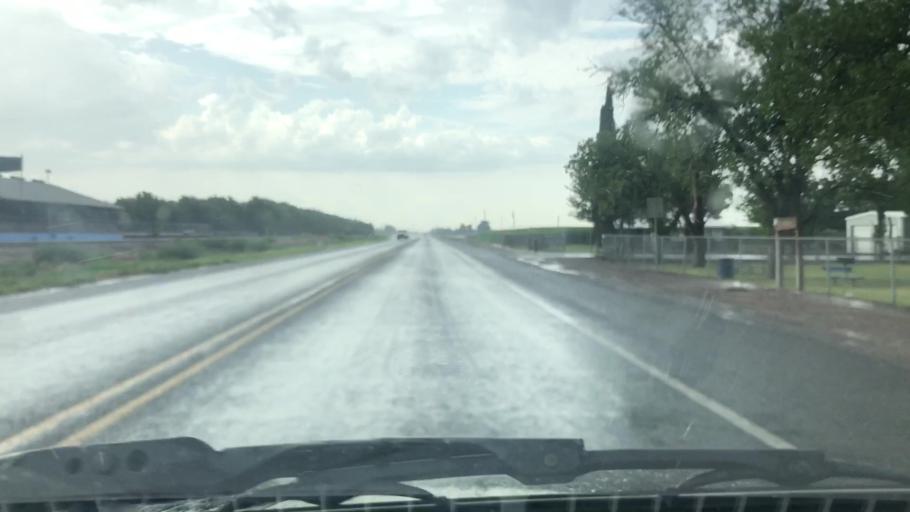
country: US
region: New Mexico
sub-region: Dona Ana County
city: Mesquite
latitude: 32.1670
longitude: -106.6981
